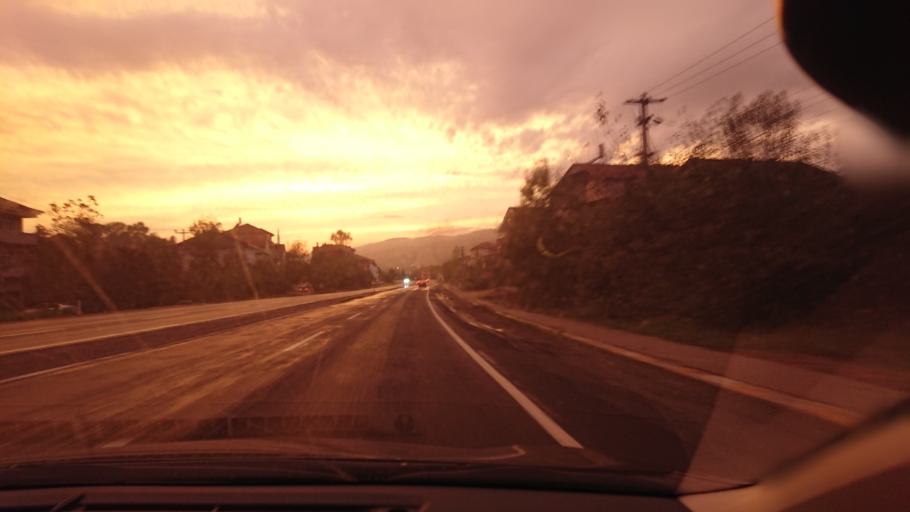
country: TR
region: Zonguldak
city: Gokcebey
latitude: 41.2797
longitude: 32.0750
